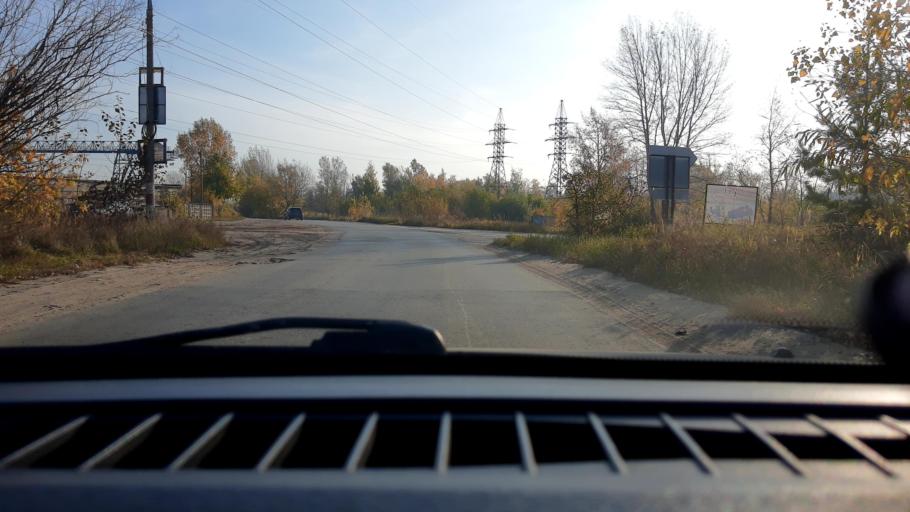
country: RU
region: Nizjnij Novgorod
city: Gorbatovka
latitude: 56.3731
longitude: 43.7966
